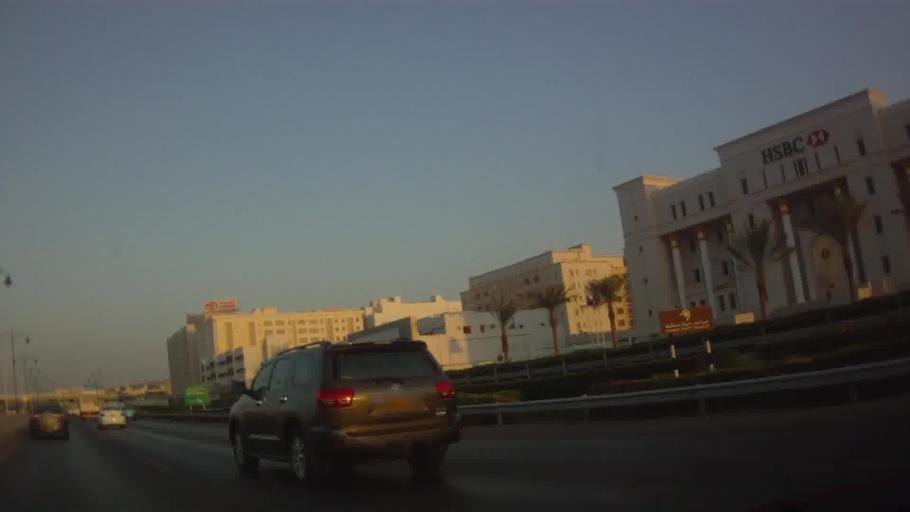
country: OM
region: Muhafazat Masqat
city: Bawshar
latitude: 23.5972
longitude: 58.4365
